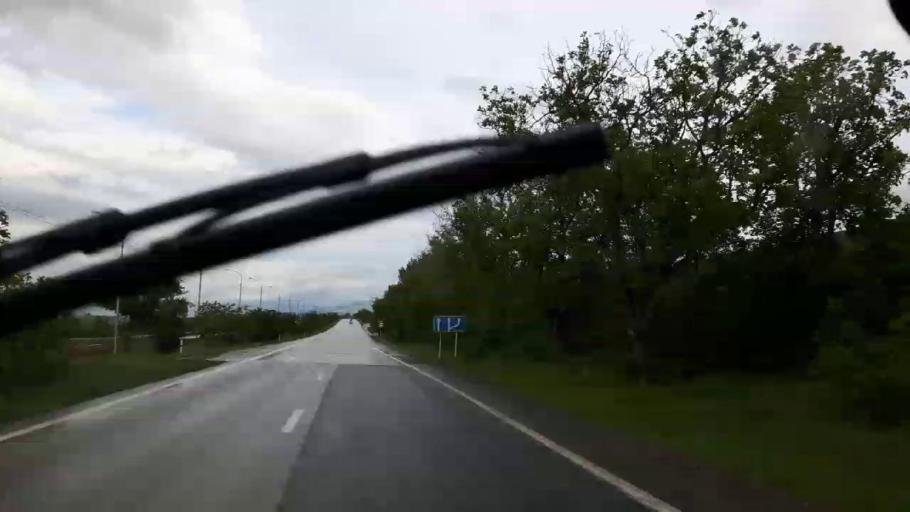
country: GE
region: Shida Kartli
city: Kaspi
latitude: 41.9652
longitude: 44.4672
